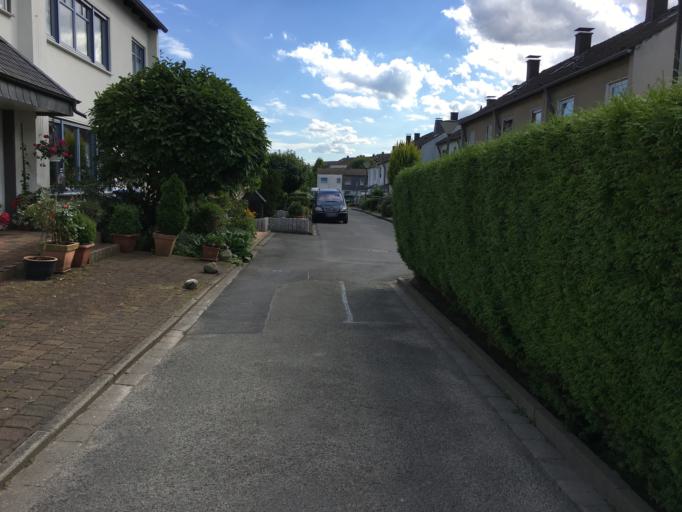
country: DE
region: North Rhine-Westphalia
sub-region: Regierungsbezirk Arnsberg
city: Frondenberg
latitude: 51.4837
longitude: 7.7237
